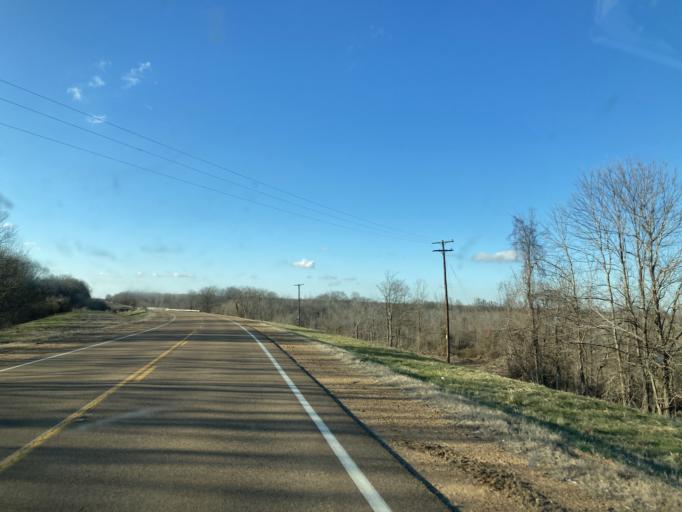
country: US
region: Mississippi
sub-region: Yazoo County
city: Yazoo City
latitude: 32.9174
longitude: -90.5554
